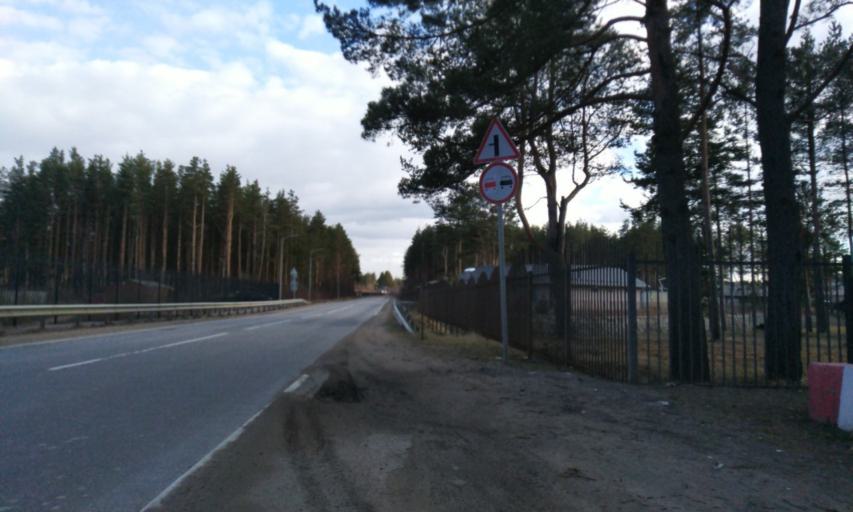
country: RU
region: Leningrad
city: Novoye Devyatkino
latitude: 60.1173
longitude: 30.4493
